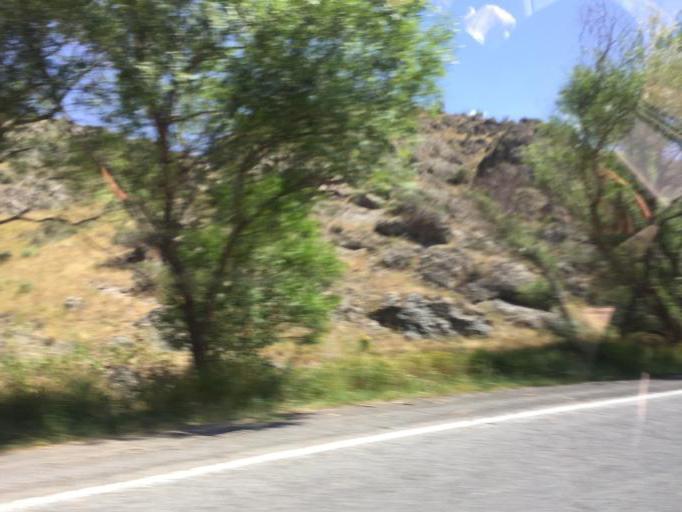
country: AM
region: Vayots' Dzori Marz
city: Jermuk
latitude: 39.7169
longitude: 45.6262
